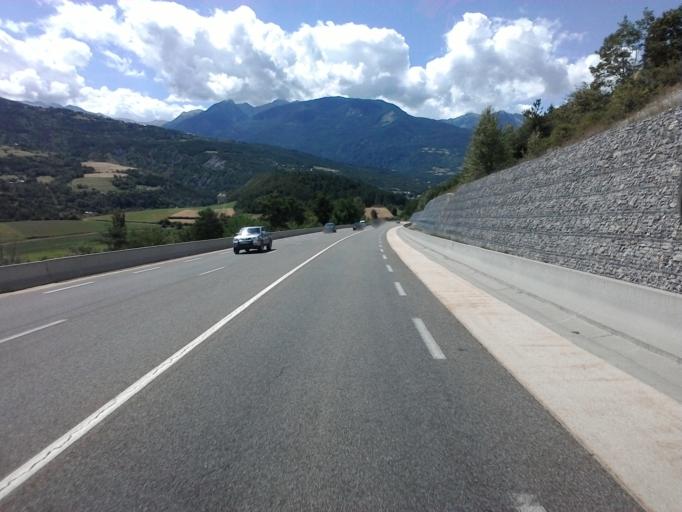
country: FR
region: Provence-Alpes-Cote d'Azur
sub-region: Departement des Hautes-Alpes
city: Embrun
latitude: 44.5746
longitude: 6.5107
